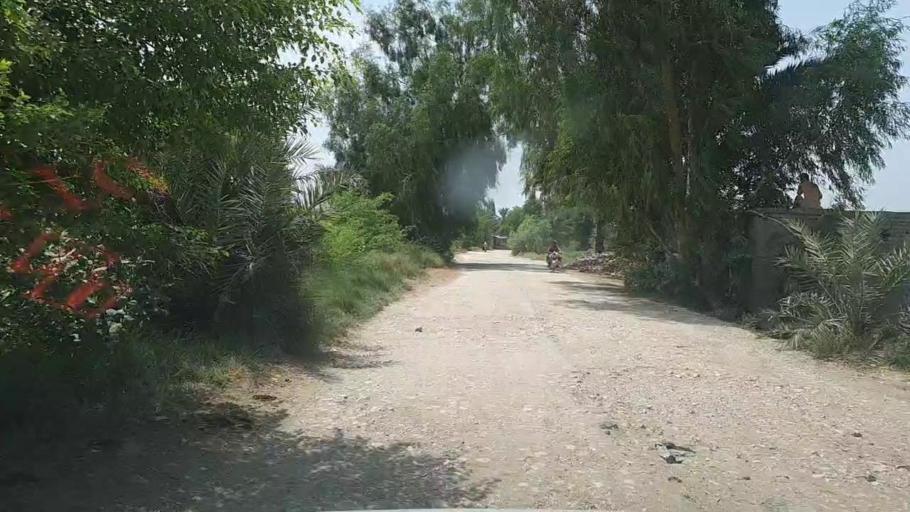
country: PK
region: Sindh
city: Pano Aqil
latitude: 27.8535
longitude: 69.1354
